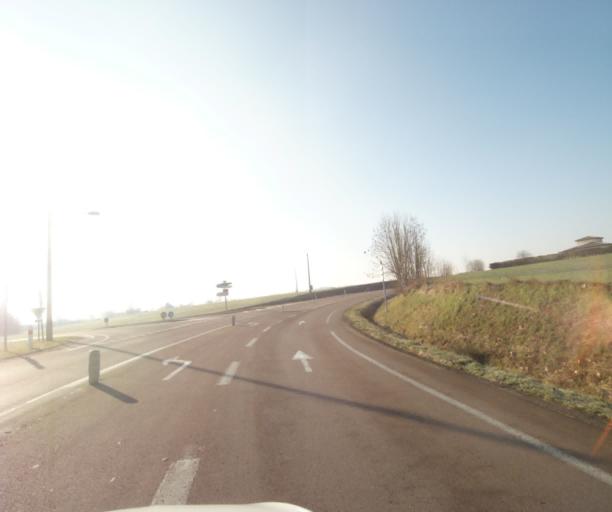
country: FR
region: Champagne-Ardenne
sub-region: Departement de la Haute-Marne
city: Montier-en-Der
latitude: 48.4654
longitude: 4.7638
